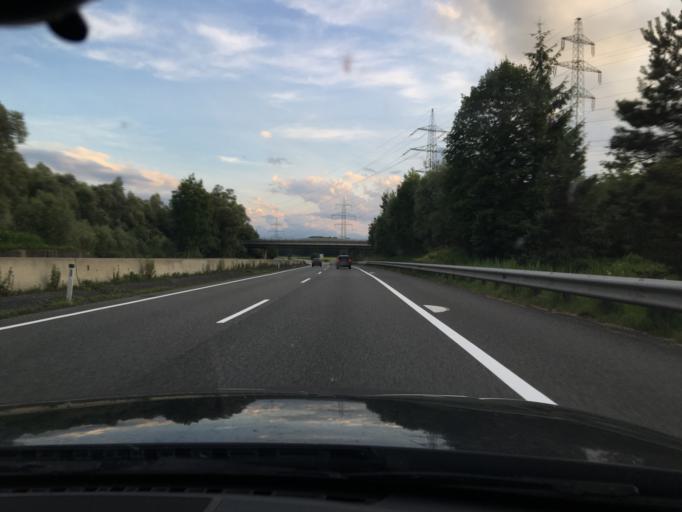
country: AT
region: Vorarlberg
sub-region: Politischer Bezirk Dornbirn
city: Hohenems
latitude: 47.3934
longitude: 9.6843
